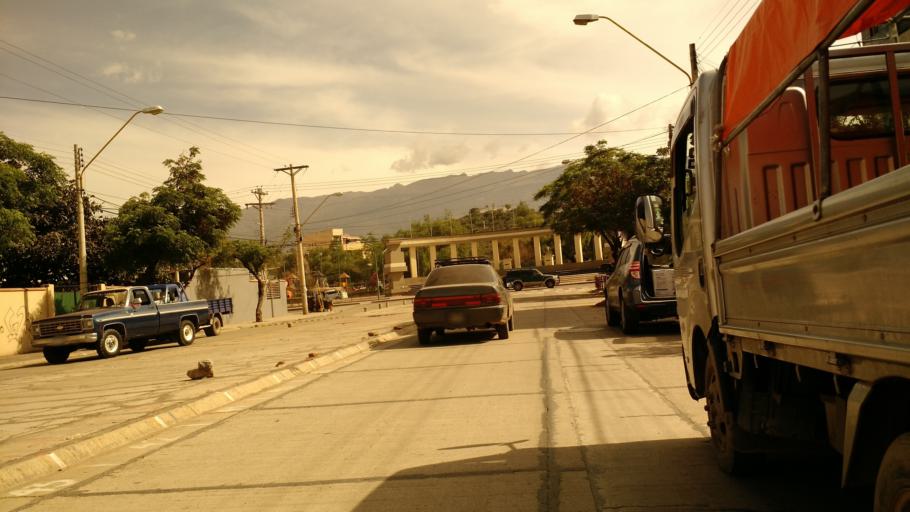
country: BO
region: Cochabamba
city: Cochabamba
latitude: -17.4139
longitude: -66.1588
